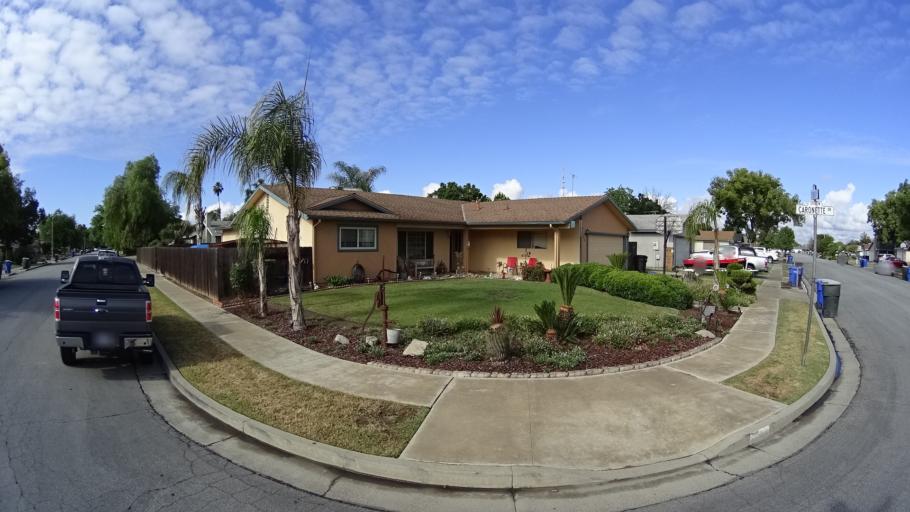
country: US
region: California
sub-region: Kings County
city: Lucerne
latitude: 36.3641
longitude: -119.6421
